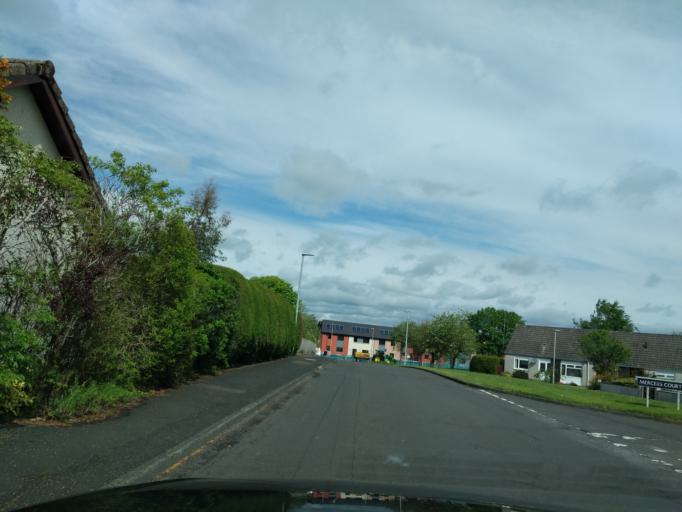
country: GB
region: Scotland
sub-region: The Scottish Borders
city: Kelso
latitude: 55.6070
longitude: -2.4388
